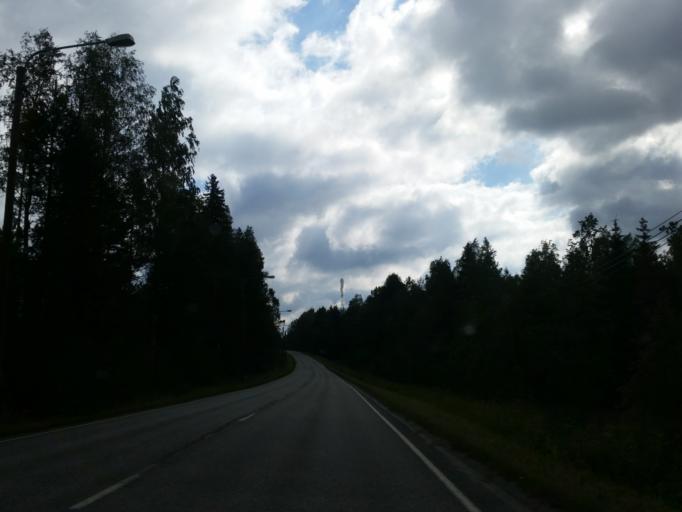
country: FI
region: Northern Savo
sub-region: Sisae-Savo
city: Suonenjoki
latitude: 62.8424
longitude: 27.3285
